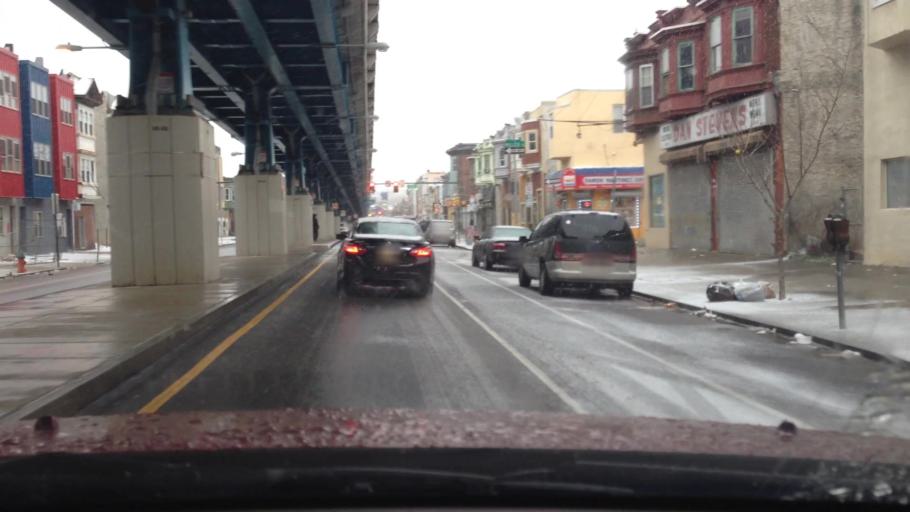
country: US
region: Pennsylvania
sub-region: Delaware County
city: Millbourne
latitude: 39.9621
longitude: -75.2415
